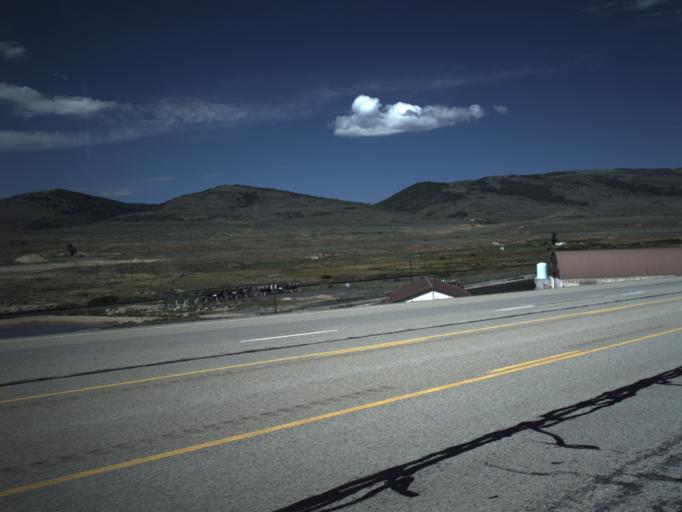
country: US
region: Utah
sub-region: Carbon County
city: Helper
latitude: 39.8512
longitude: -111.0111
